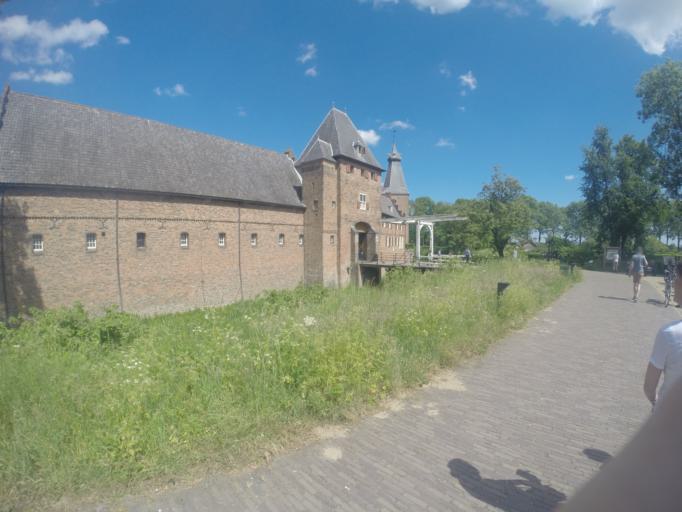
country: NL
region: Gelderland
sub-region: Gemeente Renkum
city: Doorwerth
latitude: 51.9666
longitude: 5.7874
